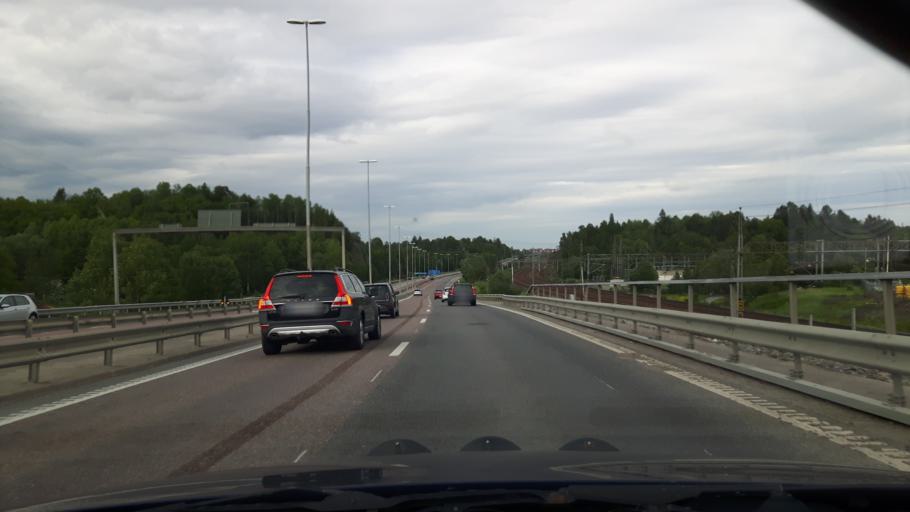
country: SE
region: Stockholm
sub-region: Huddinge Kommun
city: Huddinge
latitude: 59.2229
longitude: 17.9521
